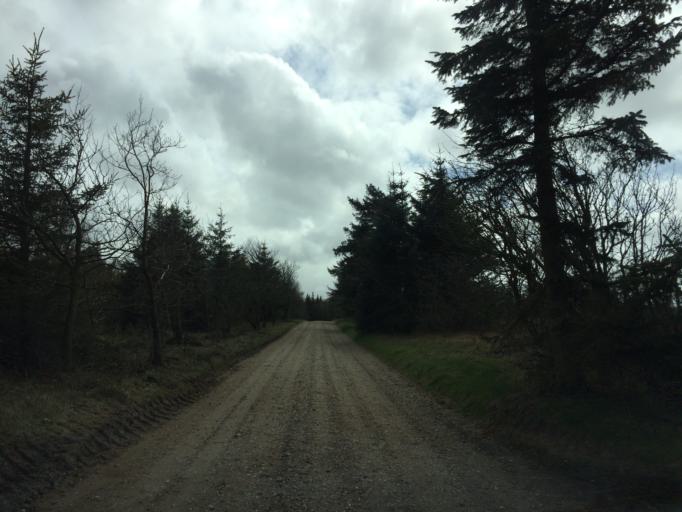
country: DK
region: South Denmark
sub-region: Varde Kommune
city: Oksbol
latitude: 55.5688
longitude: 8.3093
